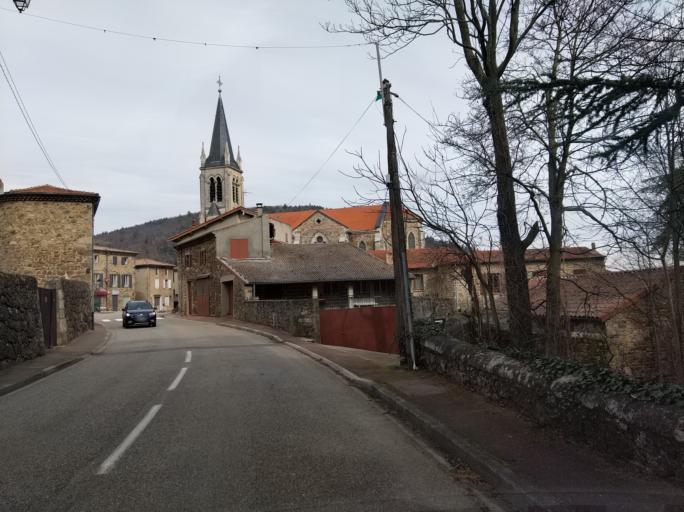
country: FR
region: Rhone-Alpes
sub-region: Departement de l'Ardeche
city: Satillieu
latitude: 45.1861
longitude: 4.6375
